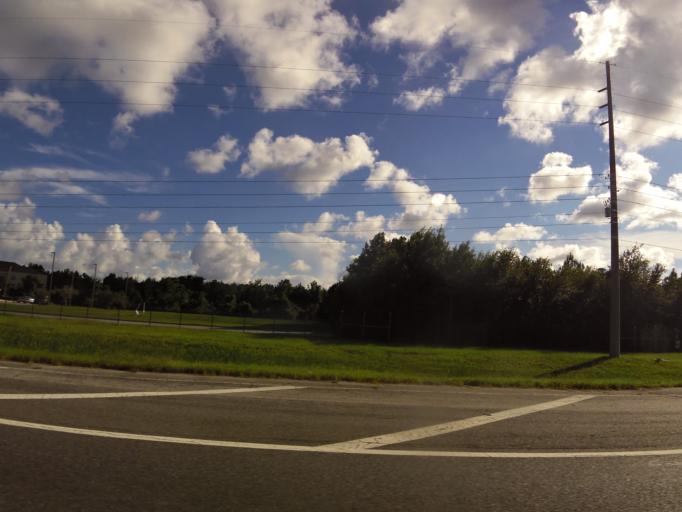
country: US
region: Georgia
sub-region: Glynn County
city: Brunswick
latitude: 31.1370
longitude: -81.5735
